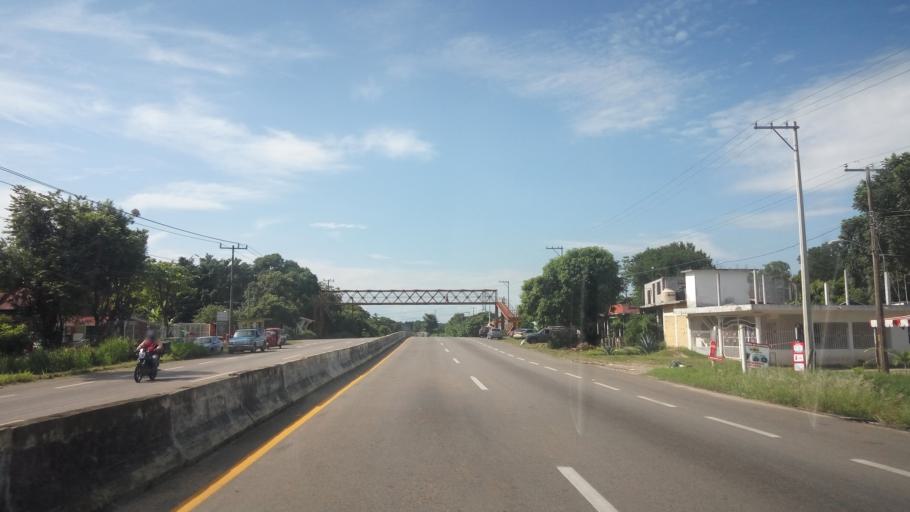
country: MX
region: Tabasco
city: Rio de Teapa
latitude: 17.8307
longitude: -92.9286
